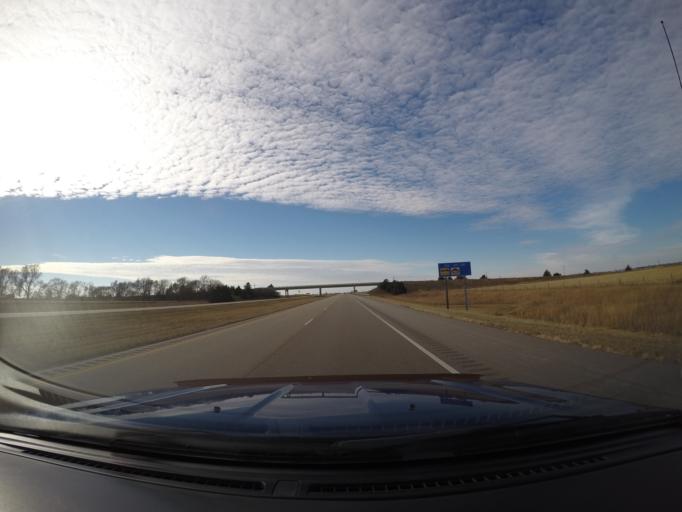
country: US
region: Nebraska
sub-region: Hamilton County
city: Aurora
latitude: 40.8223
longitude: -97.9758
